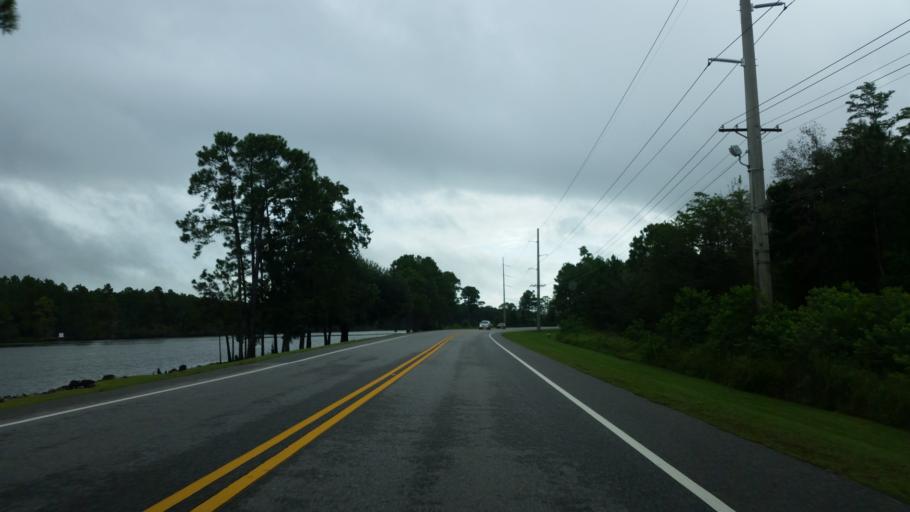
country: US
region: Alabama
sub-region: Baldwin County
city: Gulf Shores
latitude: 30.2856
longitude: -87.6450
